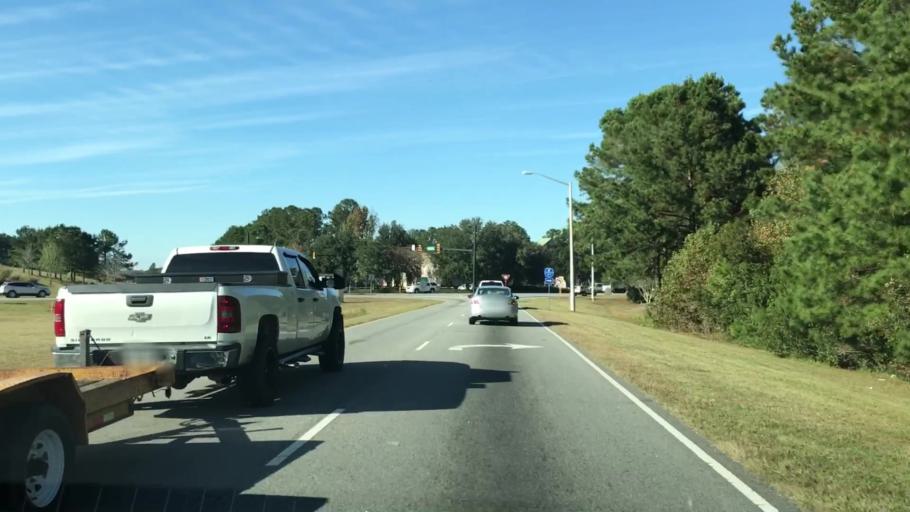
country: US
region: South Carolina
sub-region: Beaufort County
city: Bluffton
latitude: 32.2939
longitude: -80.9357
